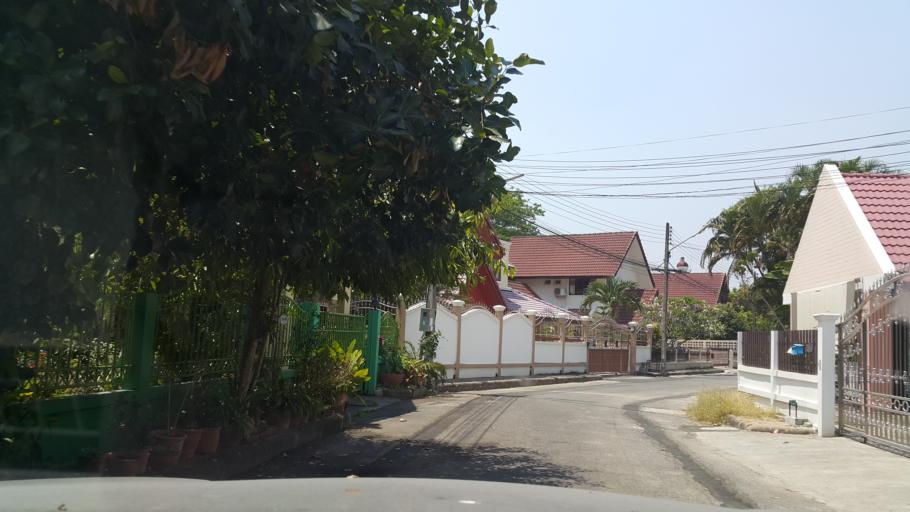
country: TH
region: Chiang Mai
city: Chiang Mai
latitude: 18.7566
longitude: 98.9906
